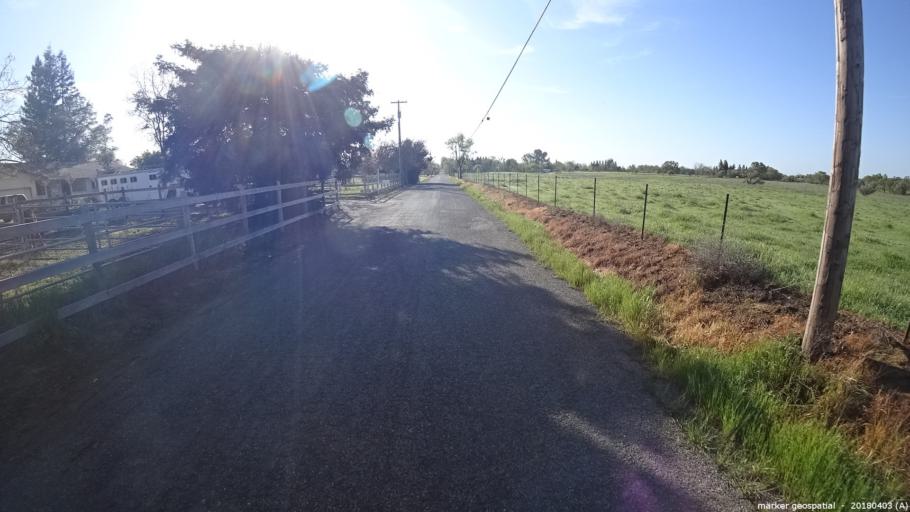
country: US
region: California
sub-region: Sacramento County
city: Wilton
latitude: 38.4437
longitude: -121.2003
